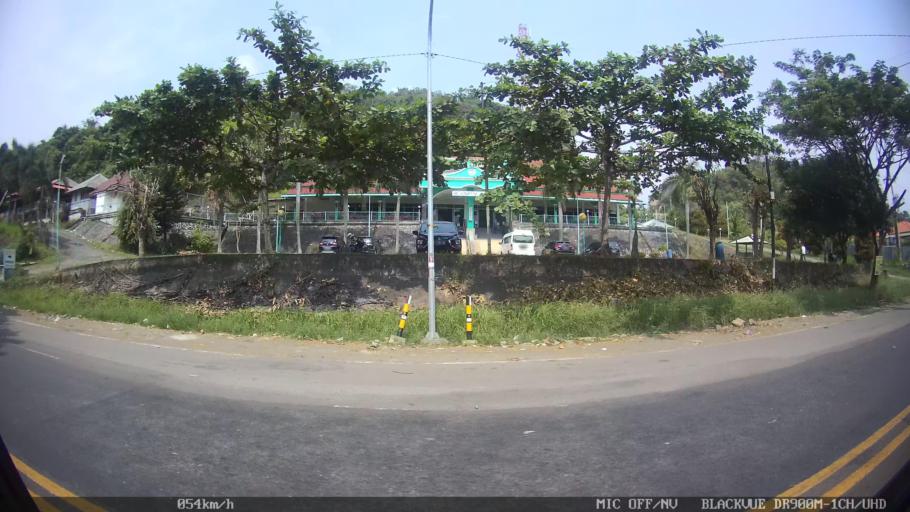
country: ID
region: Banten
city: Curug
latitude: -5.9516
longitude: 106.0015
